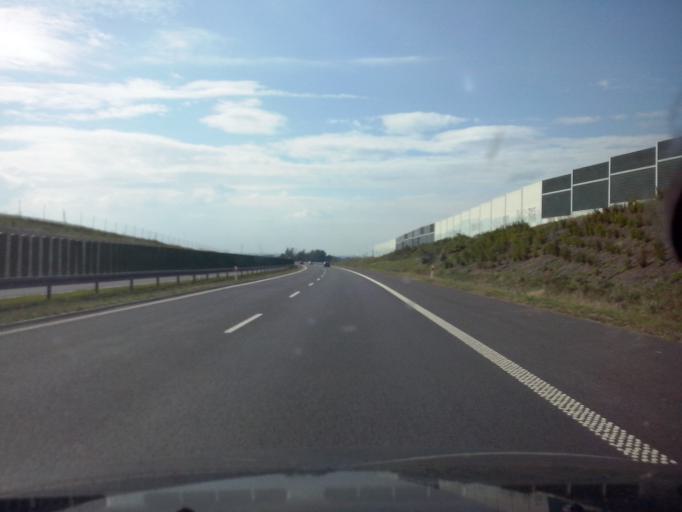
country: PL
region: Lesser Poland Voivodeship
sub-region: Powiat tarnowski
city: Lukowa
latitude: 50.0643
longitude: 20.9781
